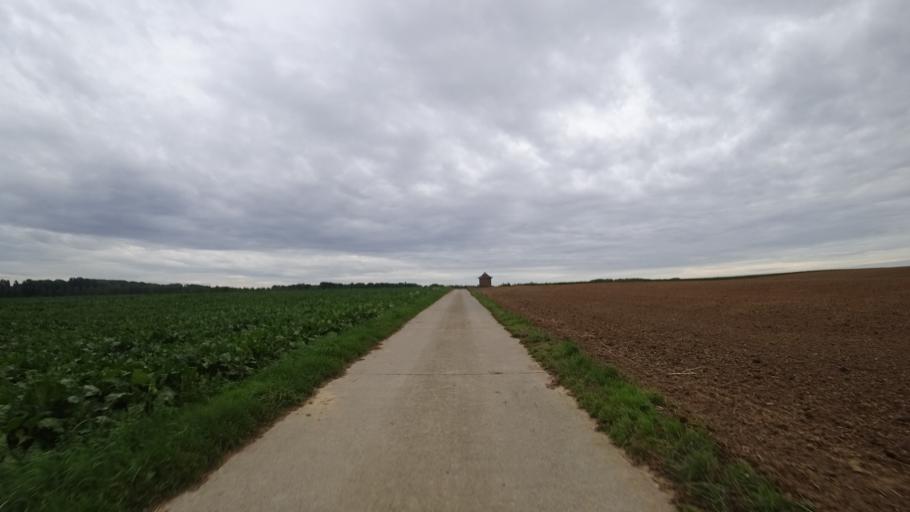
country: BE
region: Wallonia
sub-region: Province de Namur
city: Namur
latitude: 50.5385
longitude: 4.8333
